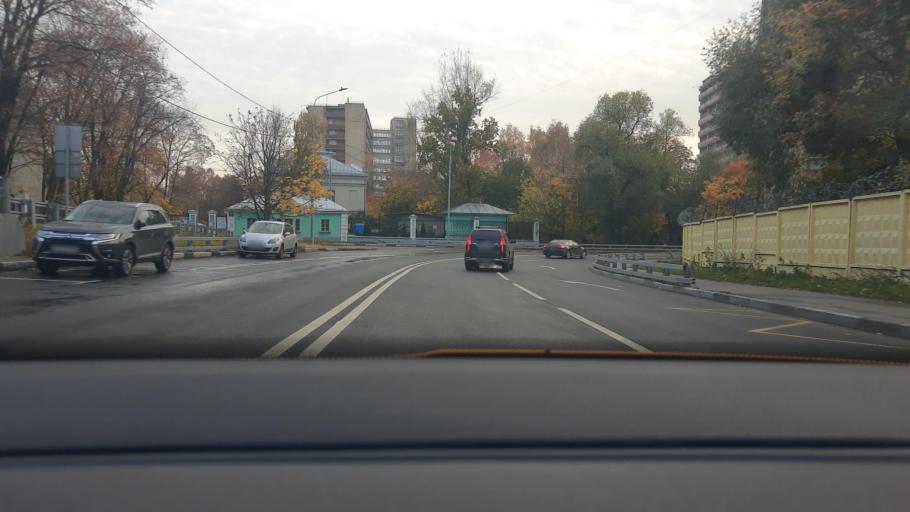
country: RU
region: Moscow
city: Khimki
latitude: 55.8817
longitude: 37.4541
